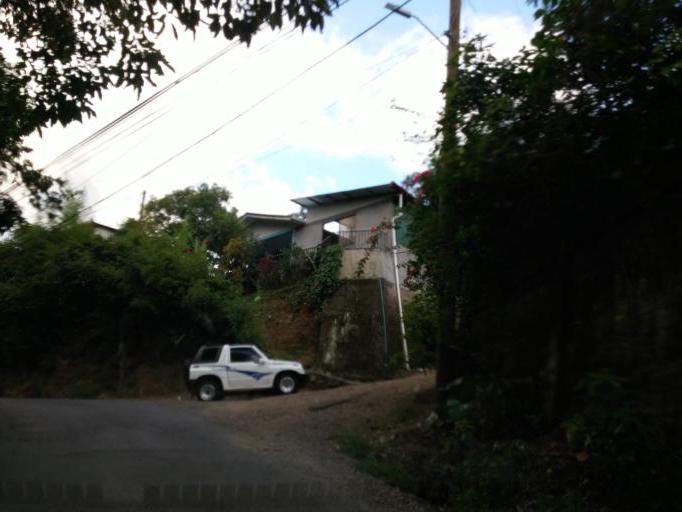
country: CR
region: San Jose
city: San Ignacio
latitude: 9.8084
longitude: -84.1808
